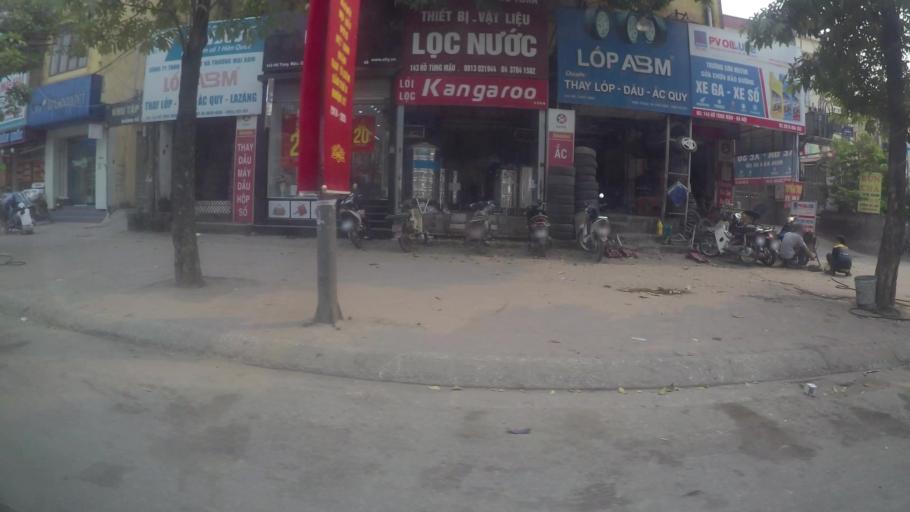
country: VN
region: Ha Noi
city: Cau Dien
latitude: 21.0400
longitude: 105.7656
